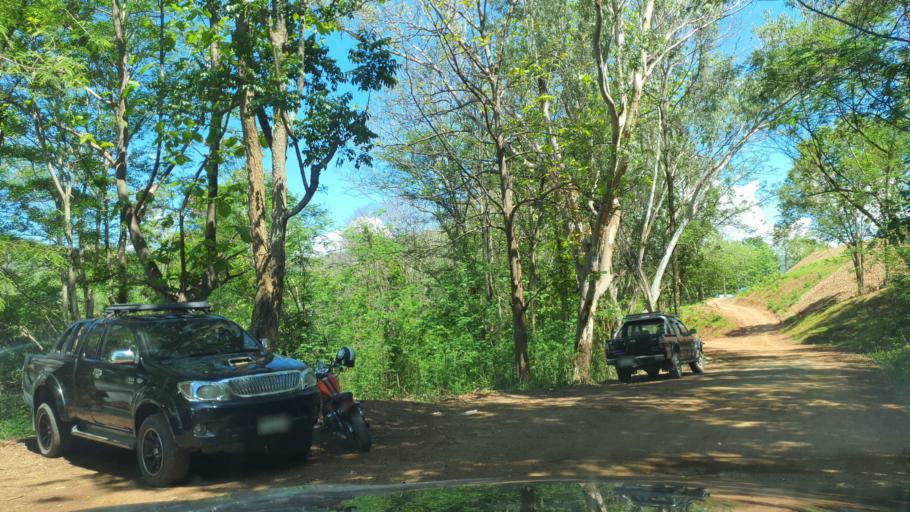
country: TH
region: Chiang Mai
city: Mae On
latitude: 18.8055
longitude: 99.2649
